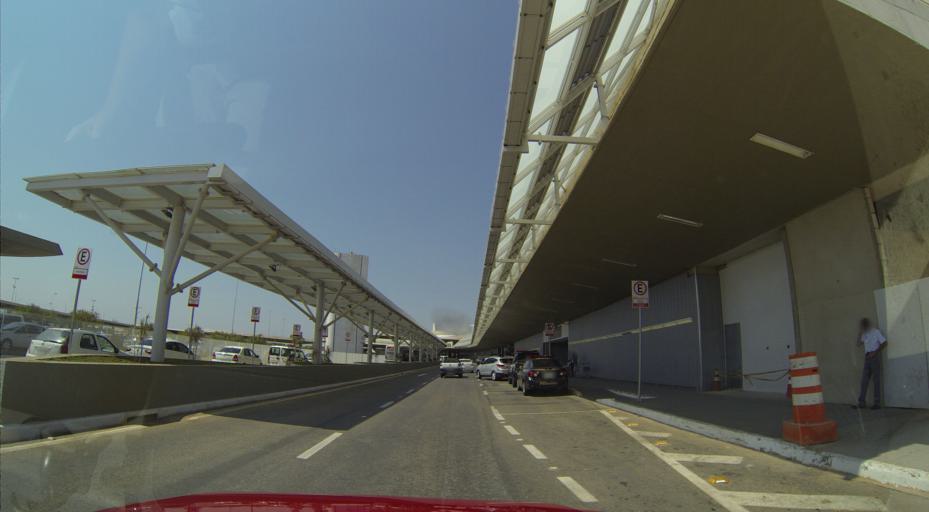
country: BR
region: Minas Gerais
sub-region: Lagoa Santa
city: Lagoa Santa
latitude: -19.6283
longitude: -43.9658
